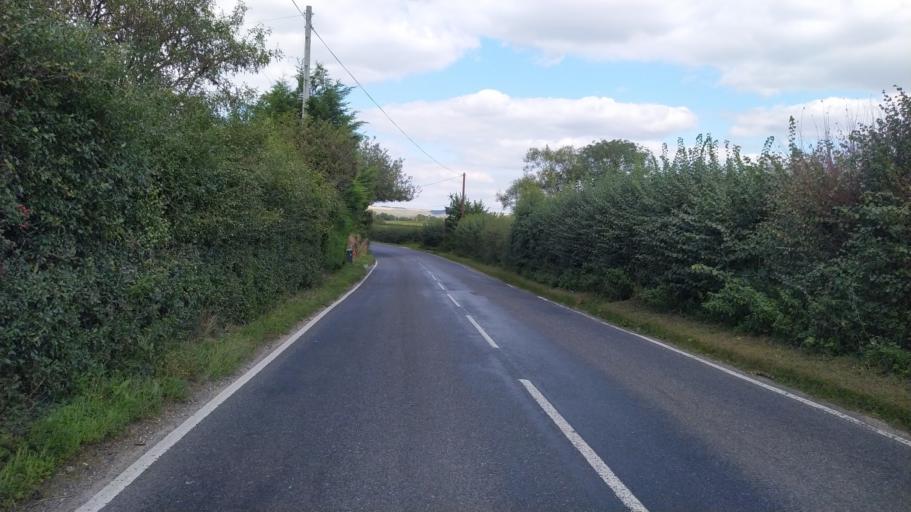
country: GB
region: England
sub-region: Dorset
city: Gillingham
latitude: 51.0580
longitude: -2.2841
